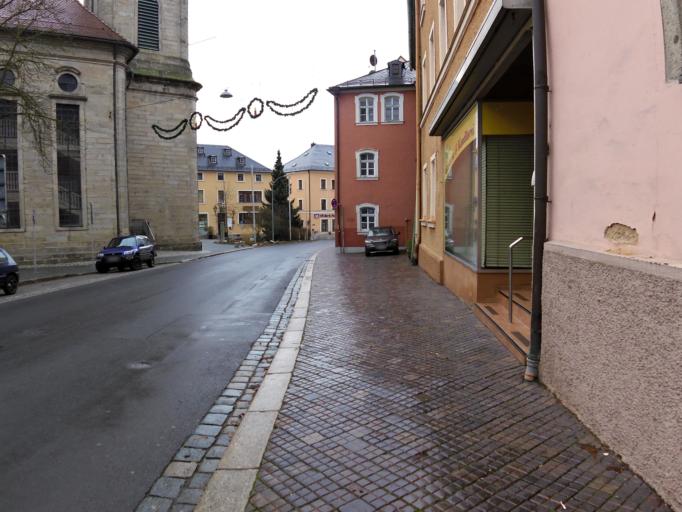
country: DE
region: Bavaria
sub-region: Upper Franconia
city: Wunsiedel
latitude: 50.0384
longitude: 12.0040
